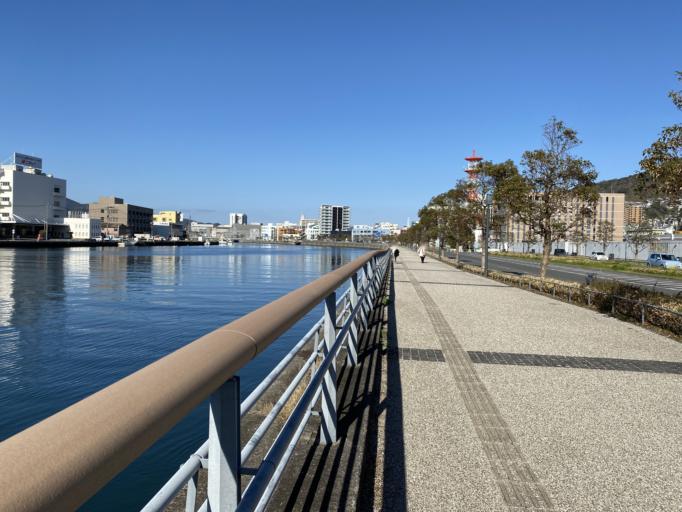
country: JP
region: Nagasaki
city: Nagasaki-shi
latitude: 32.7516
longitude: 129.8668
